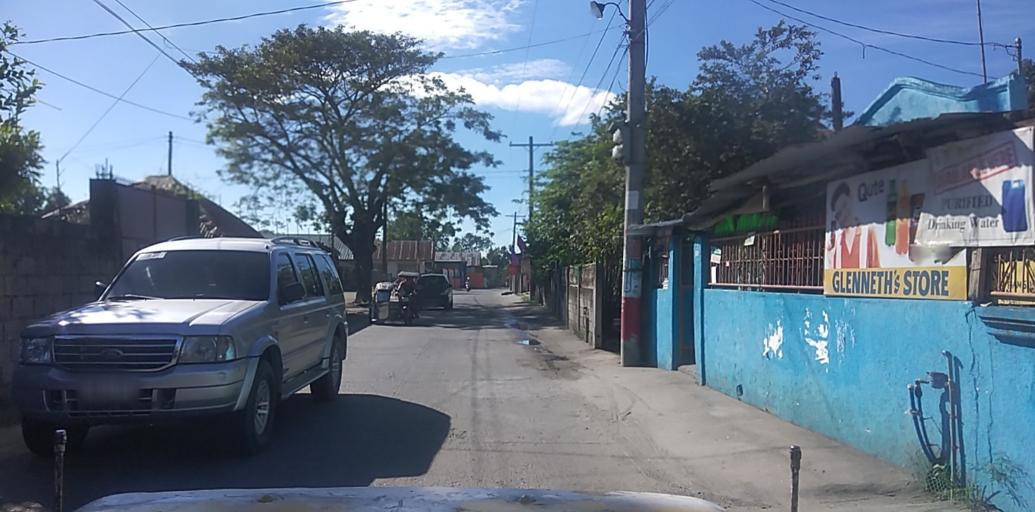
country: PH
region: Central Luzon
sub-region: Province of Pampanga
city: San Patricio
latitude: 15.0983
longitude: 120.7138
